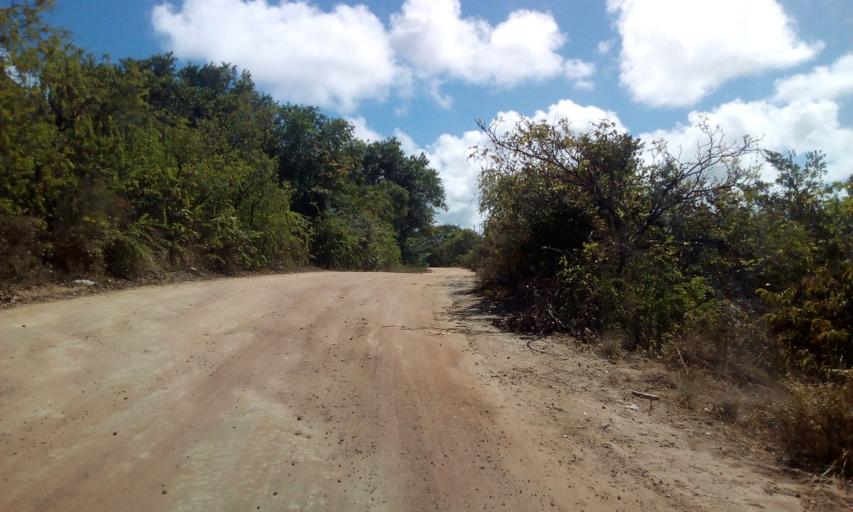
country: BR
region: Paraiba
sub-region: Conde
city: Conde
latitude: -7.2759
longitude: -34.8017
